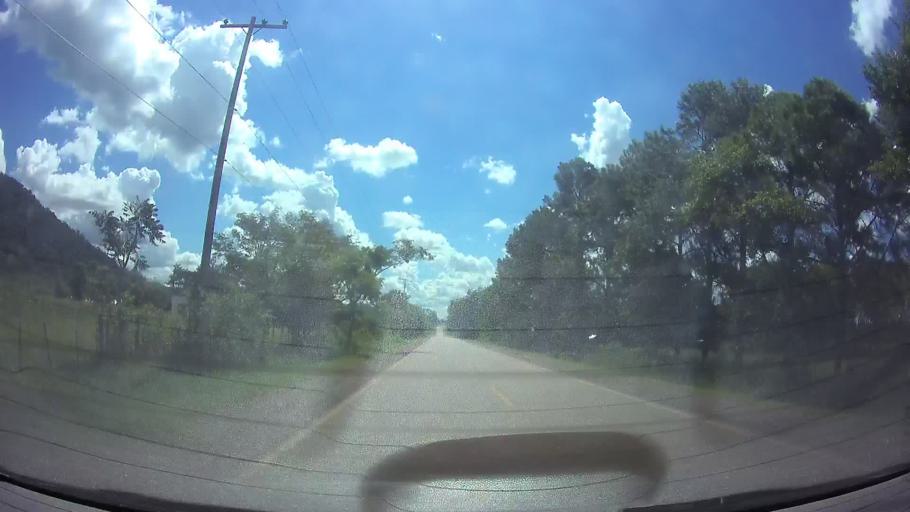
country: PY
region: Paraguari
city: La Colmena
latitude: -25.9134
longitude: -56.7492
